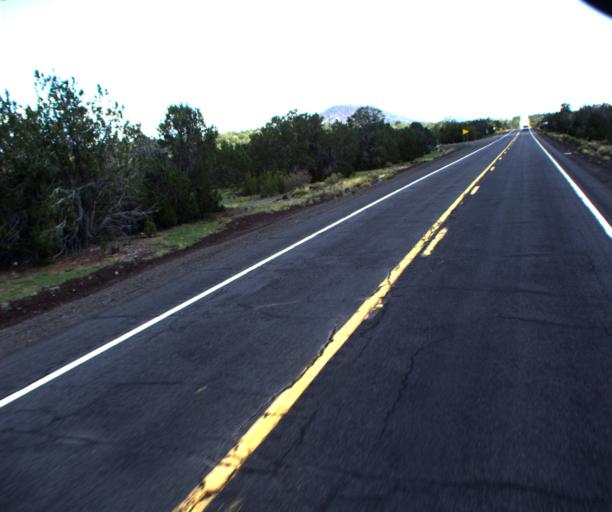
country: US
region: Arizona
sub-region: Coconino County
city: Williams
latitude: 35.4339
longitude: -112.1712
